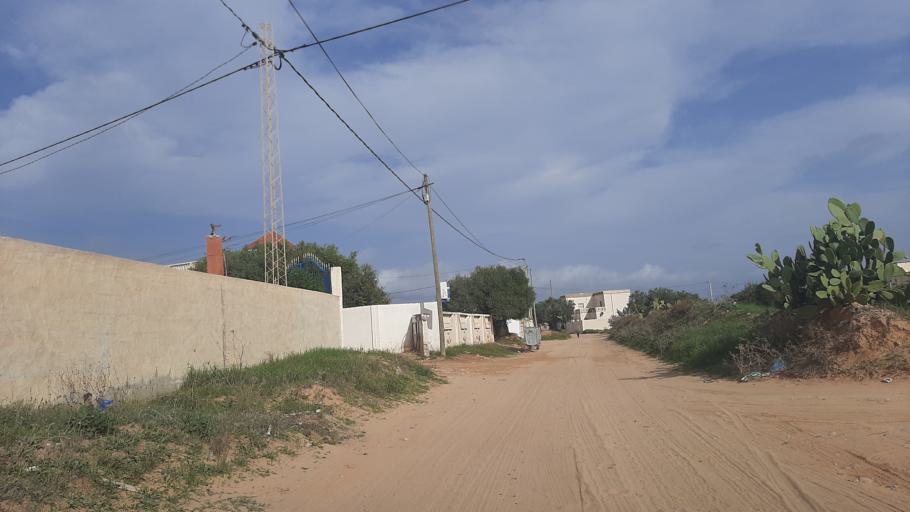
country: TN
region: Madanin
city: Midoun
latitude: 33.8117
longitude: 11.0255
